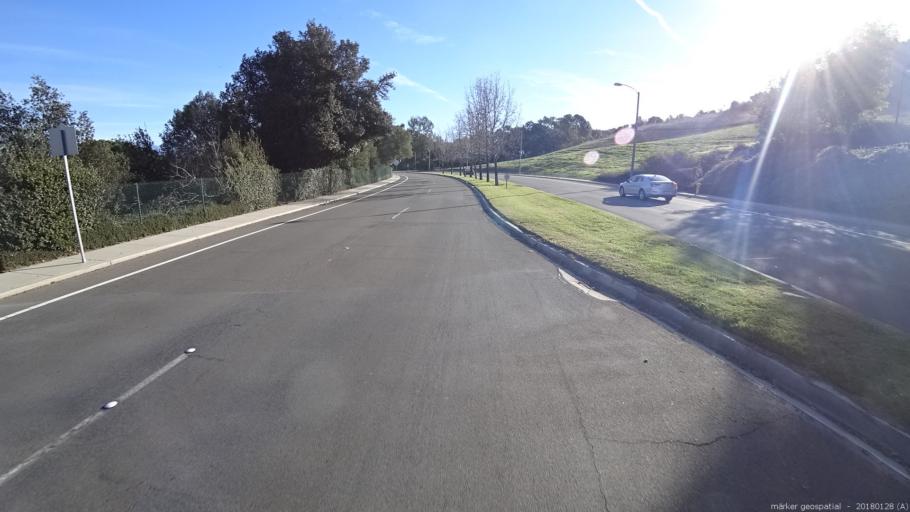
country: US
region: California
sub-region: Los Angeles County
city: Diamond Bar
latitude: 34.0027
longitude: -117.8270
